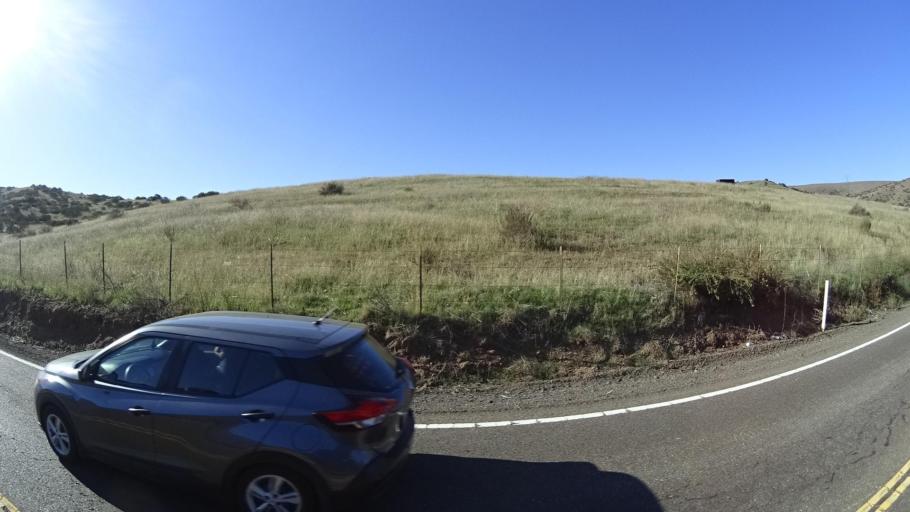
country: US
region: California
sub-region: San Diego County
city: Jamul
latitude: 32.6541
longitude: -116.8048
